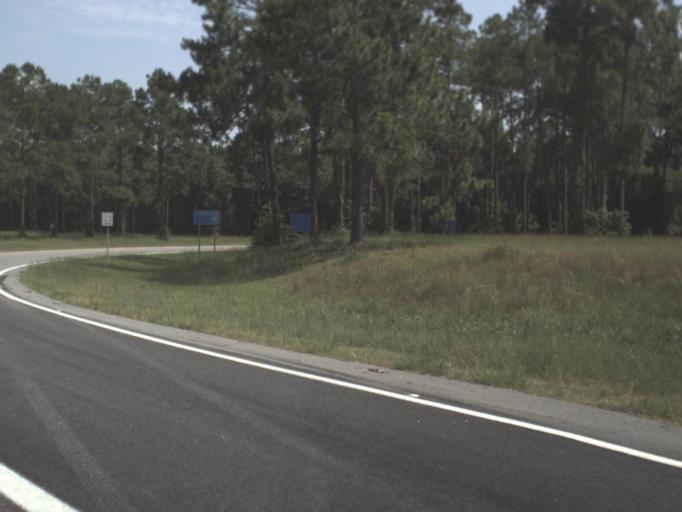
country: US
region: Georgia
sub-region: Echols County
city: Statenville
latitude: 30.5947
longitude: -83.1199
